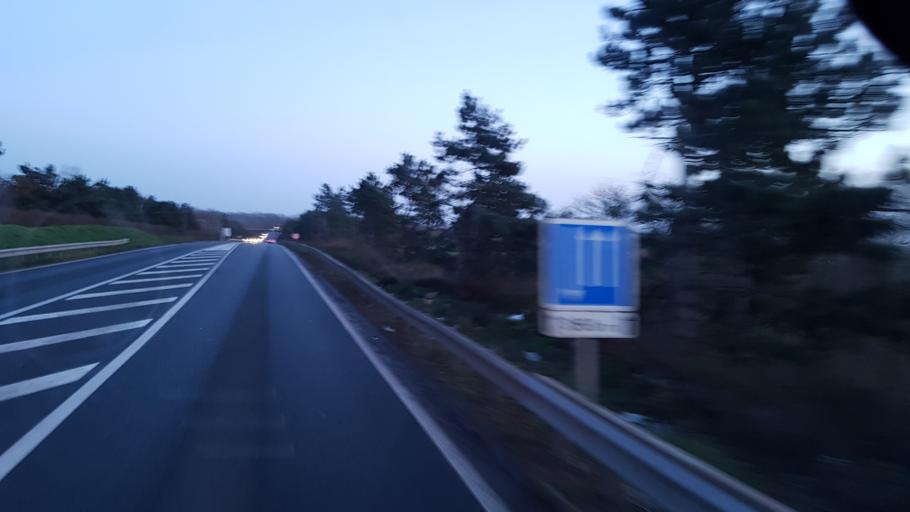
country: FR
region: Nord-Pas-de-Calais
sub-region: Departement du Nord
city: Lambres-lez-Douai
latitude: 50.3485
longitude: 3.0655
